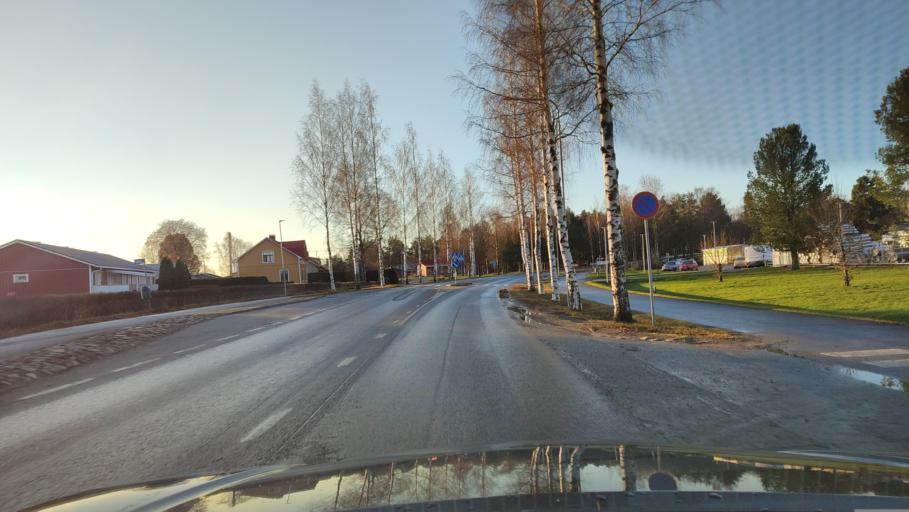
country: FI
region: Ostrobothnia
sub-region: Sydosterbotten
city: Naerpes
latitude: 62.4706
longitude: 21.3353
